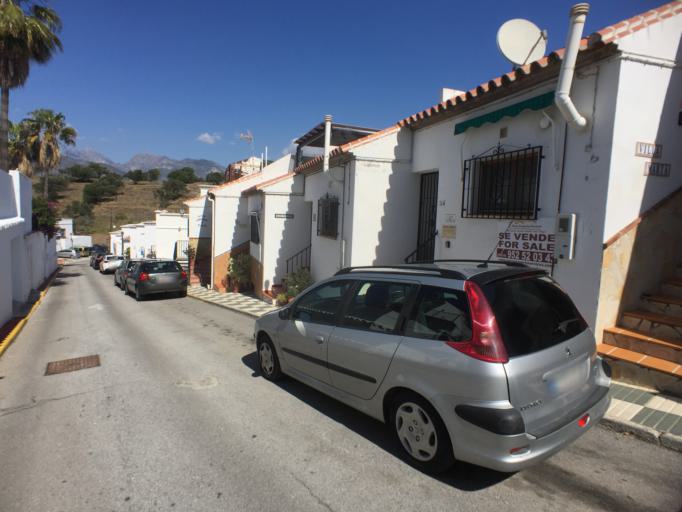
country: ES
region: Andalusia
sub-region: Provincia de Malaga
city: Nerja
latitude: 36.7475
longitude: -3.9046
